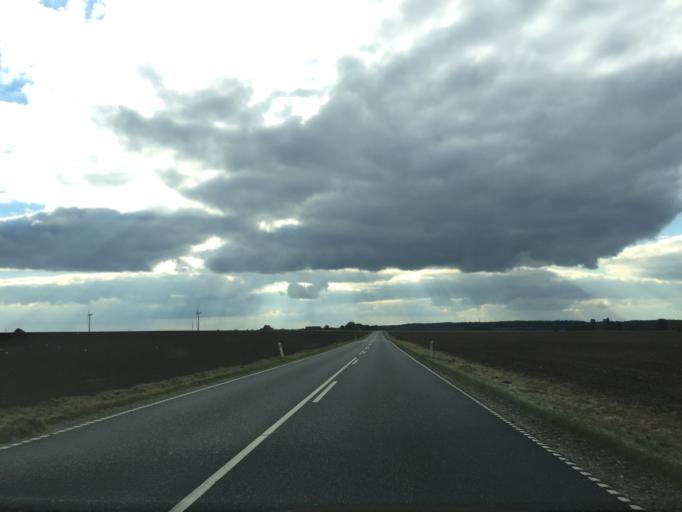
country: DK
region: Central Jutland
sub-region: Randers Kommune
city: Langa
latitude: 56.3415
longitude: 9.8678
